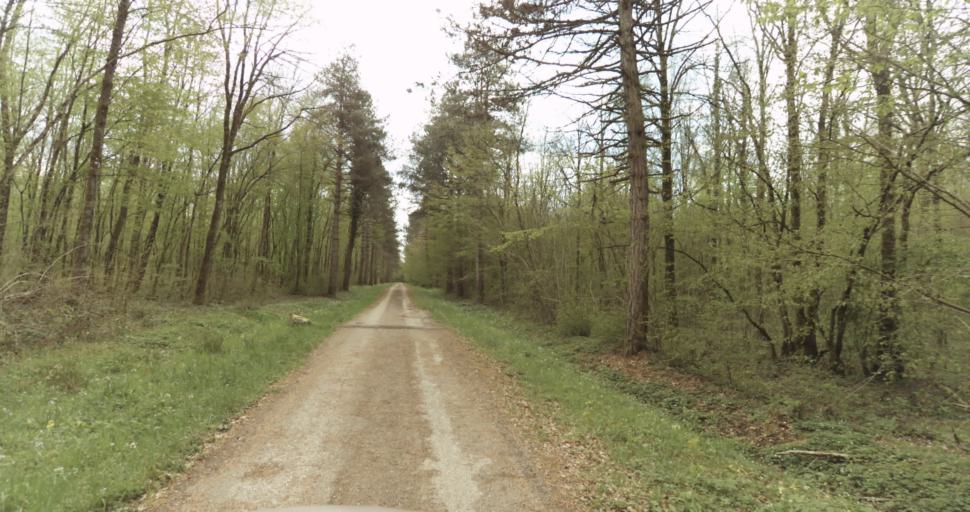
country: FR
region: Bourgogne
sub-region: Departement de la Cote-d'Or
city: Auxonne
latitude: 47.1573
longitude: 5.4225
